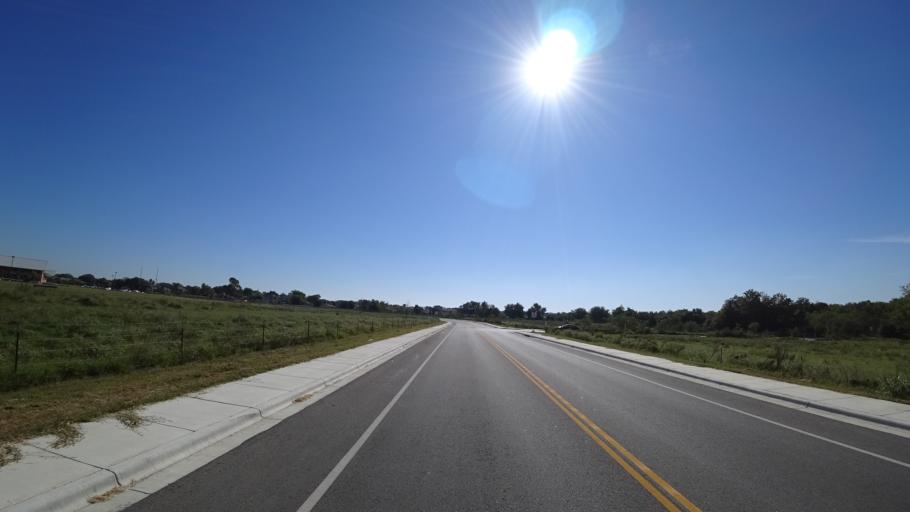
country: US
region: Texas
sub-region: Travis County
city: Hornsby Bend
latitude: 30.2414
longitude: -97.5915
